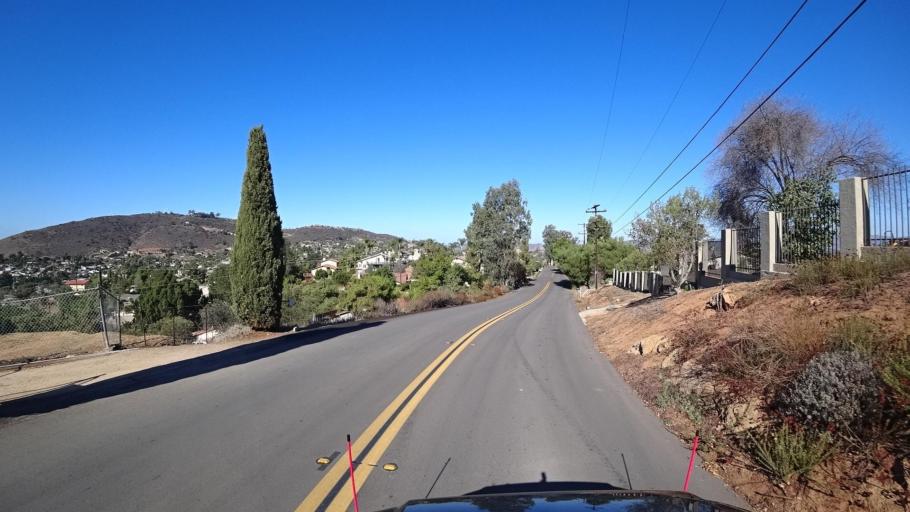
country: US
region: California
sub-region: San Diego County
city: Winter Gardens
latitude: 32.8311
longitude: -116.9267
